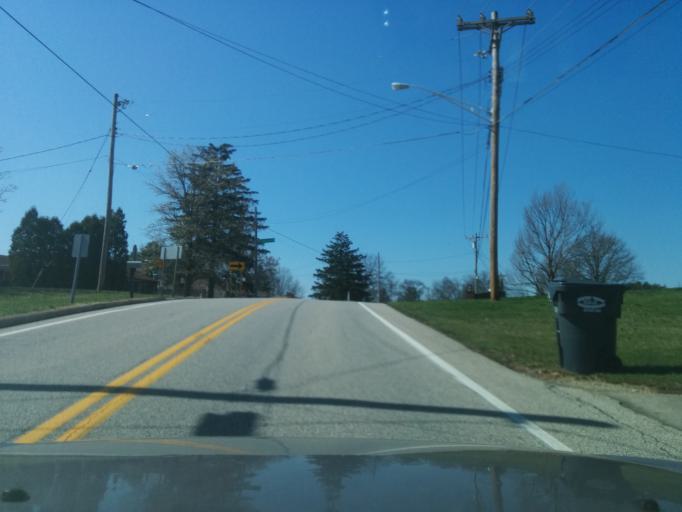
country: US
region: Ohio
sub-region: Hamilton County
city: Cheviot
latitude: 39.1805
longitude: -84.6225
